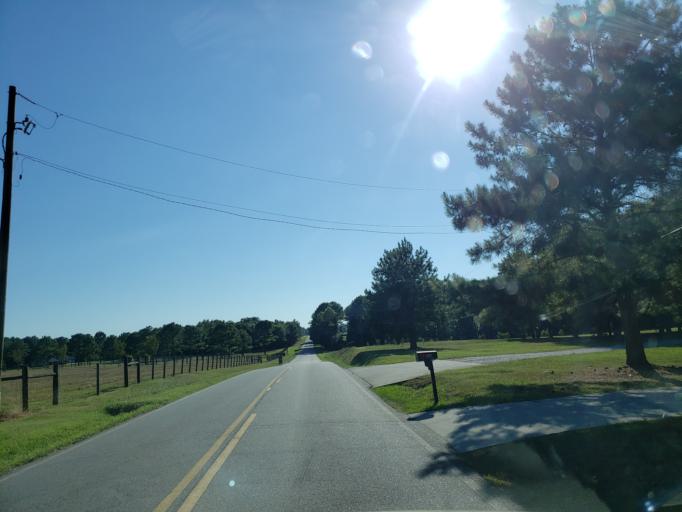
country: US
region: Georgia
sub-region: Bartow County
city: Euharlee
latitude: 34.1054
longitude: -84.9650
